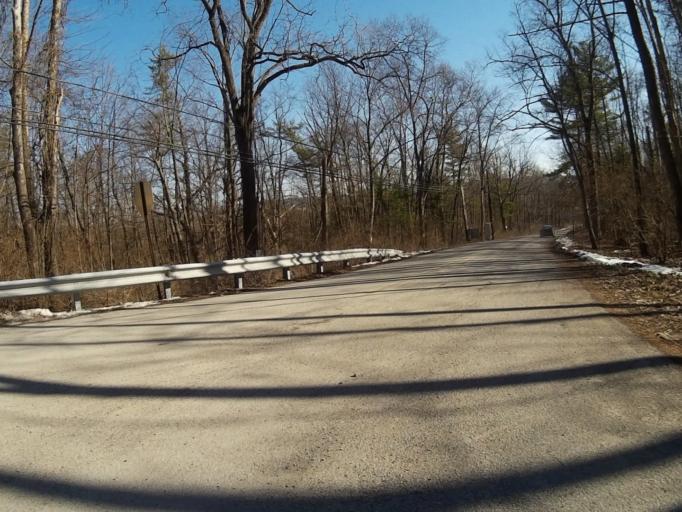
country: US
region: Pennsylvania
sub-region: Centre County
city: Houserville
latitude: 40.8787
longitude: -77.8708
